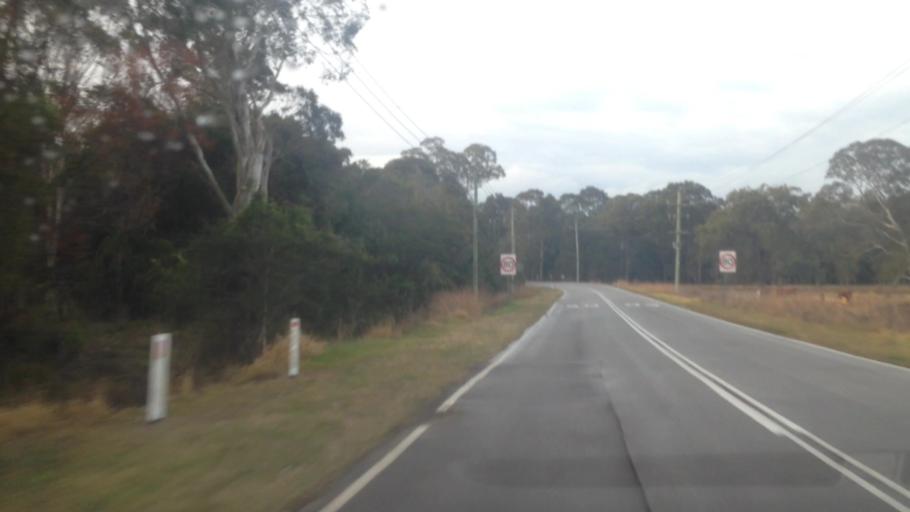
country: AU
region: New South Wales
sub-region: Wyong Shire
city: Charmhaven
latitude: -33.1657
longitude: 151.4773
